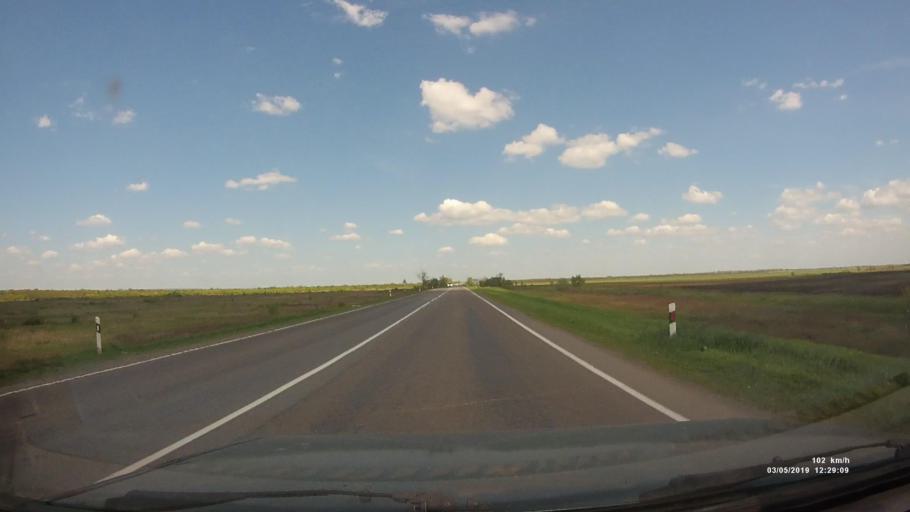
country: RU
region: Rostov
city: Semikarakorsk
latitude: 47.4845
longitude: 40.7361
